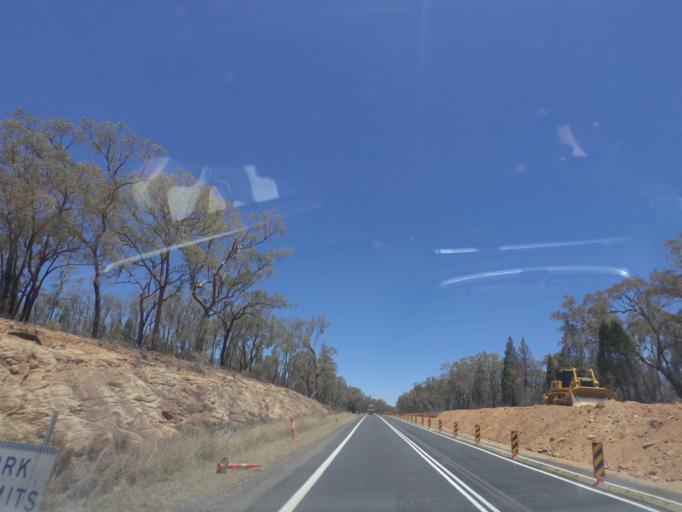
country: AU
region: New South Wales
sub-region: Warrumbungle Shire
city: Coonabarabran
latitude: -30.9234
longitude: 149.4319
